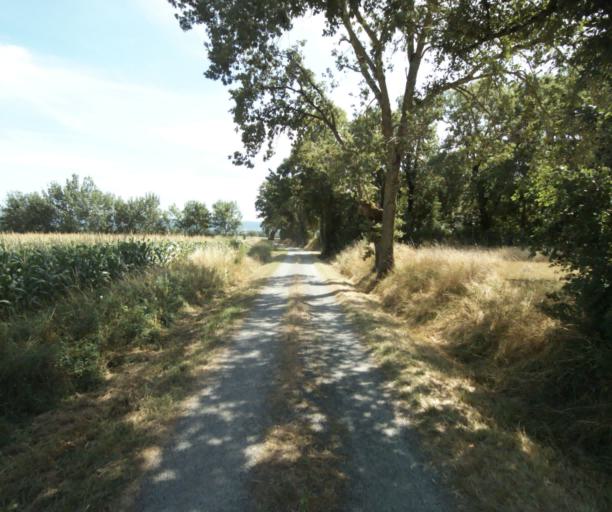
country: FR
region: Midi-Pyrenees
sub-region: Departement du Tarn
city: Puylaurens
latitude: 43.5293
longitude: 2.0289
